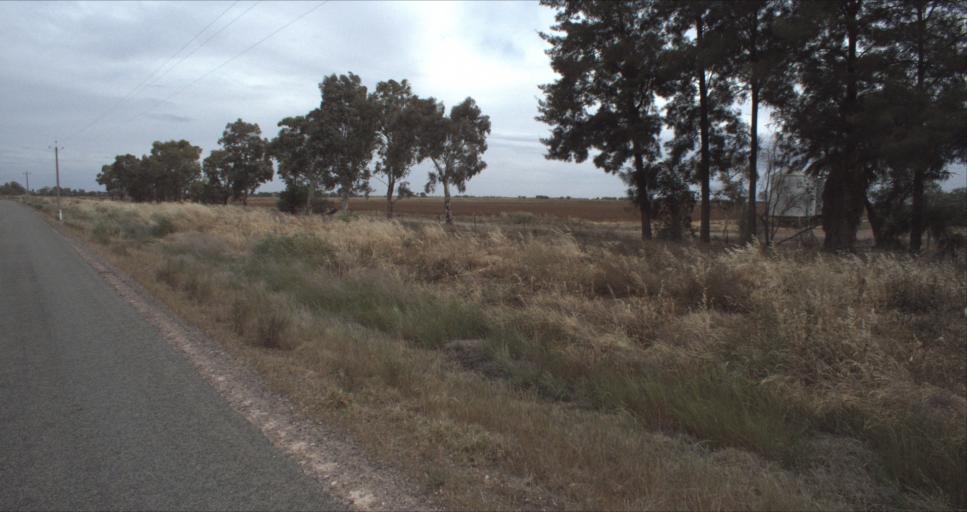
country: AU
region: New South Wales
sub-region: Leeton
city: Leeton
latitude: -34.4324
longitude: 146.3770
